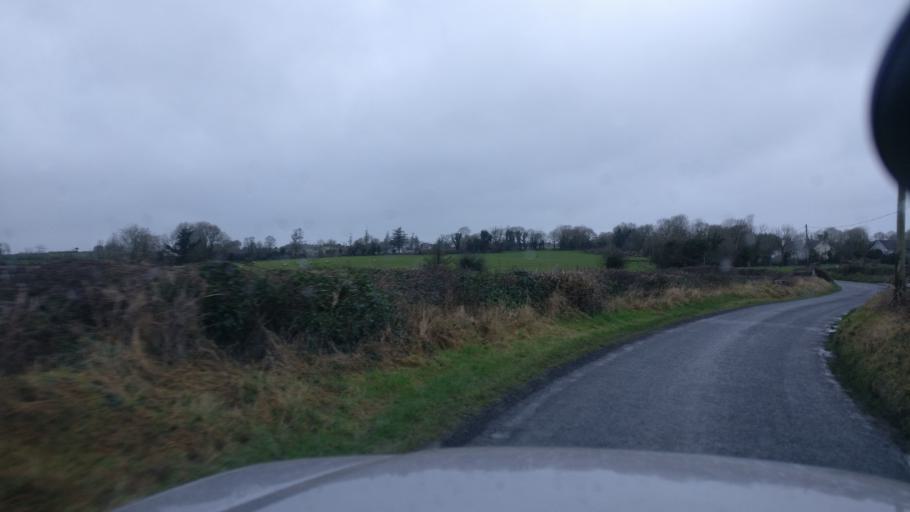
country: IE
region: Connaught
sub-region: County Galway
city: Loughrea
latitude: 53.1990
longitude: -8.6566
